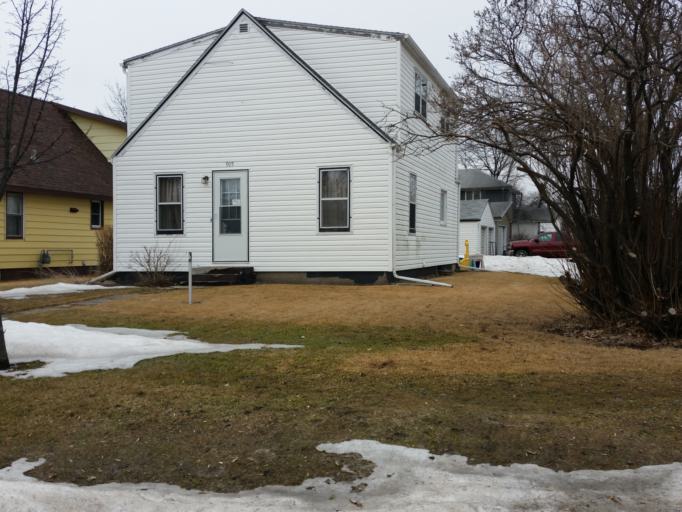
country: US
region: North Dakota
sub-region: Walsh County
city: Grafton
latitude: 48.4155
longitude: -97.4202
